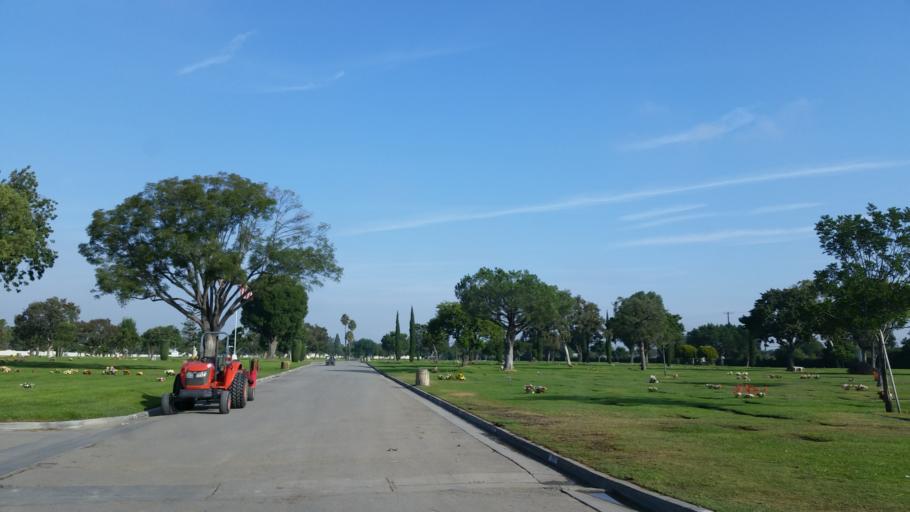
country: US
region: California
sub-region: Los Angeles County
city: Signal Hill
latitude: 33.8373
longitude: -118.1655
